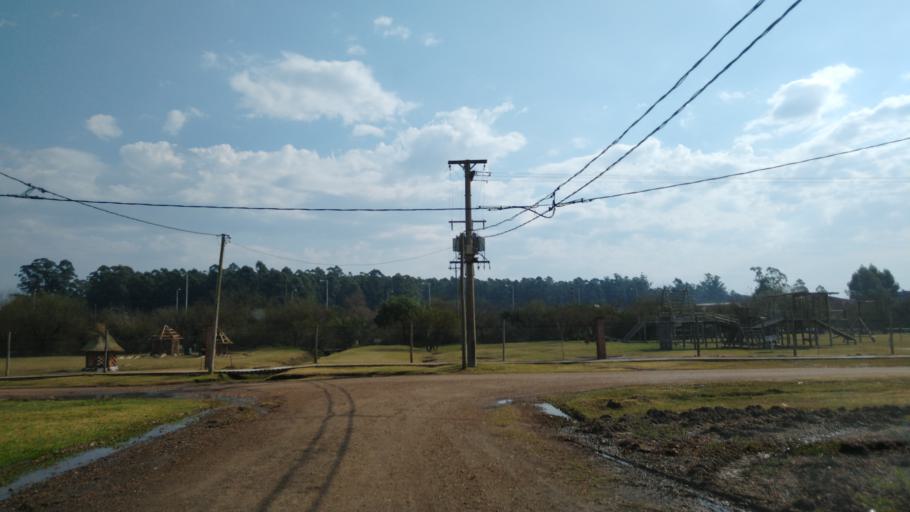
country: AR
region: Entre Rios
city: Chajari
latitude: -30.7423
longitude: -58.0139
